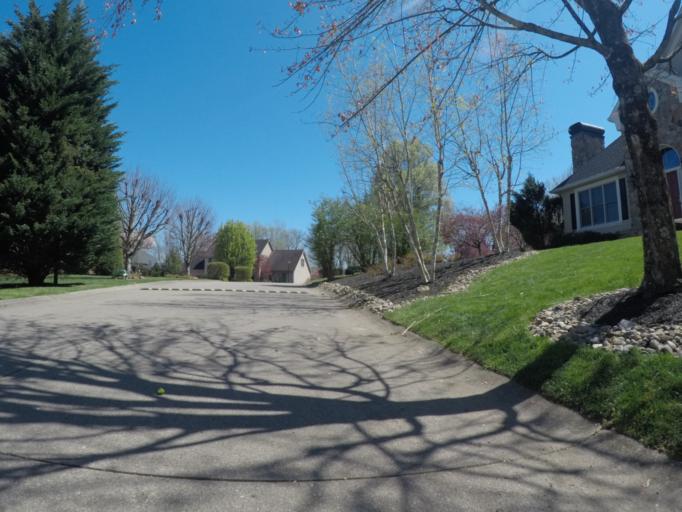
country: US
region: West Virginia
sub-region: Cabell County
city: Pea Ridge
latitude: 38.4183
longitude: -82.3146
